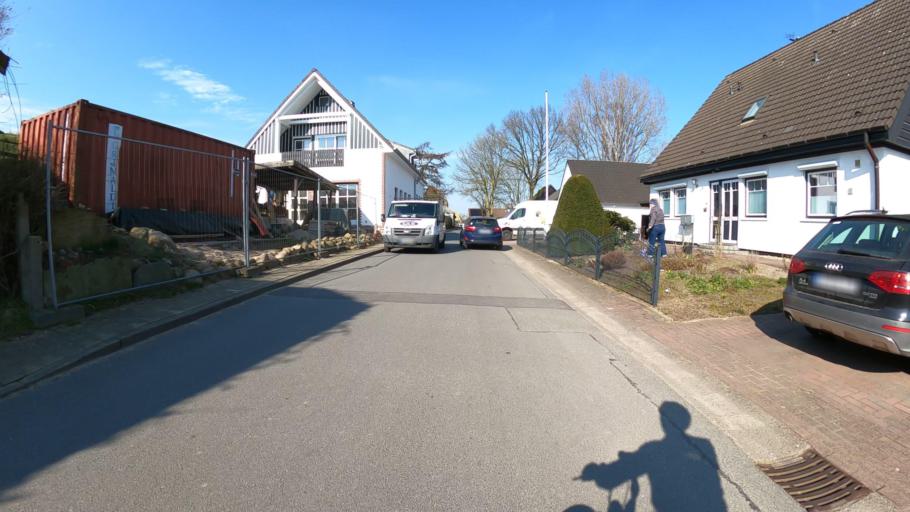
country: DE
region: Schleswig-Holstein
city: Seestermuhe
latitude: 53.7008
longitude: 9.5636
